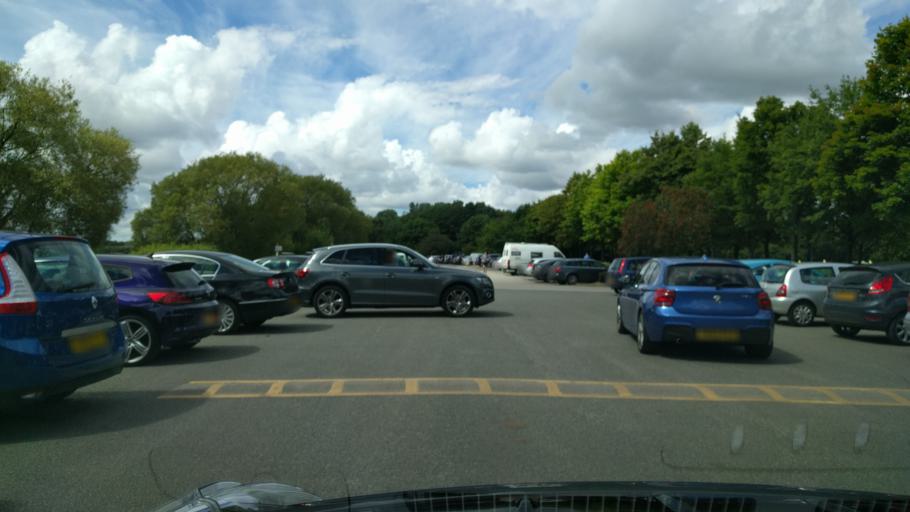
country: GB
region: England
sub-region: Borough of Wigan
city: Leigh
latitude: 53.4861
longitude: -2.5366
